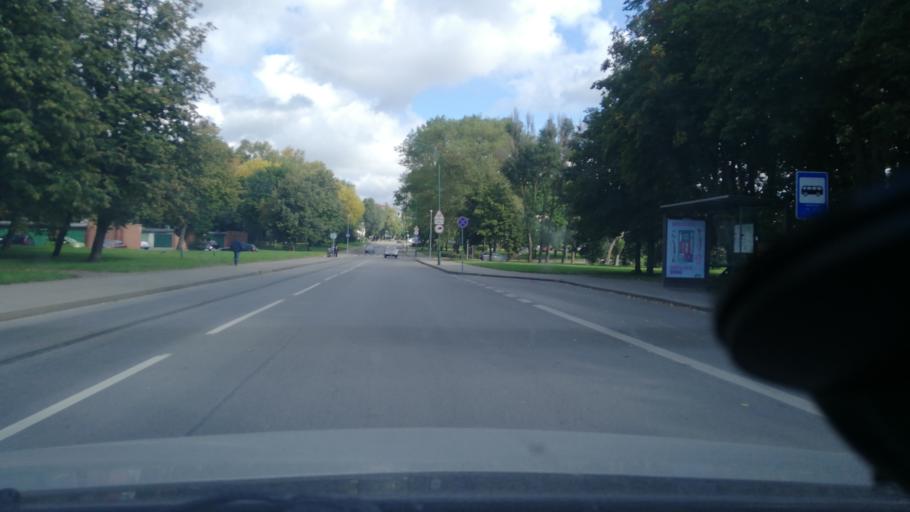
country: LT
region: Klaipedos apskritis
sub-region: Klaipeda
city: Klaipeda
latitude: 55.6827
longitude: 21.1731
